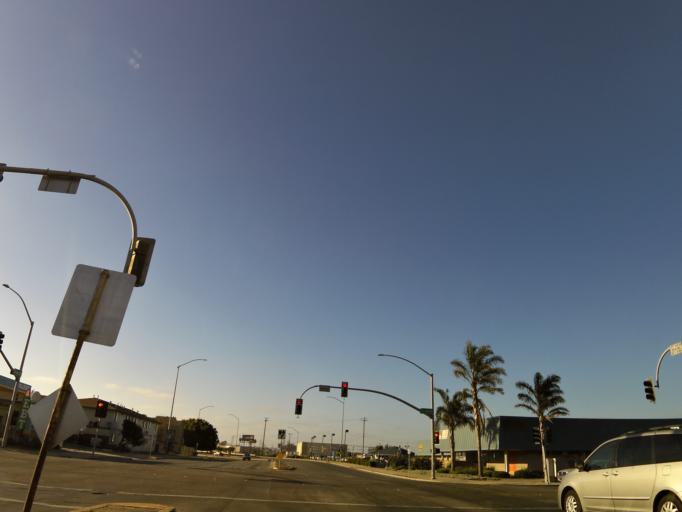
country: US
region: California
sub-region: Monterey County
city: Salinas
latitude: 36.6744
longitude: -121.6491
